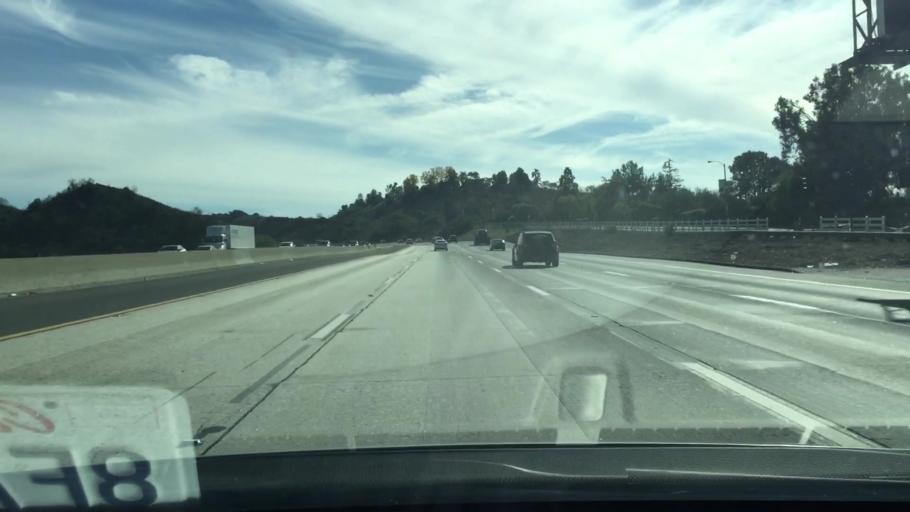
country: US
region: California
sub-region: Los Angeles County
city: San Dimas
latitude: 34.0883
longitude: -117.8197
